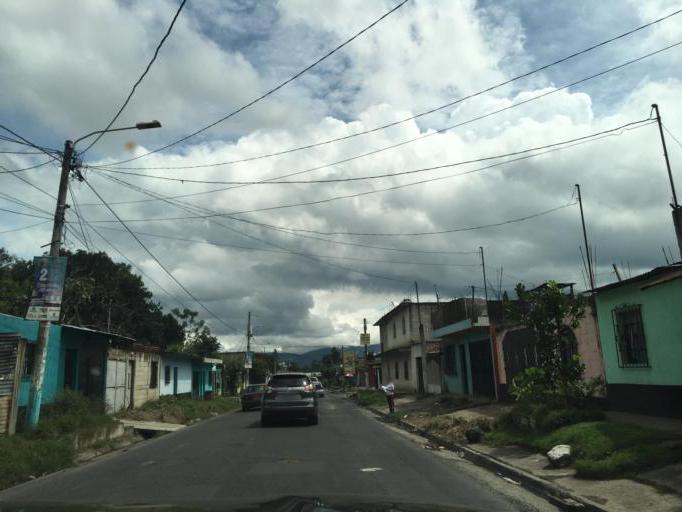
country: GT
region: Guatemala
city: Villa Nueva
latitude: 14.5069
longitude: -90.5853
